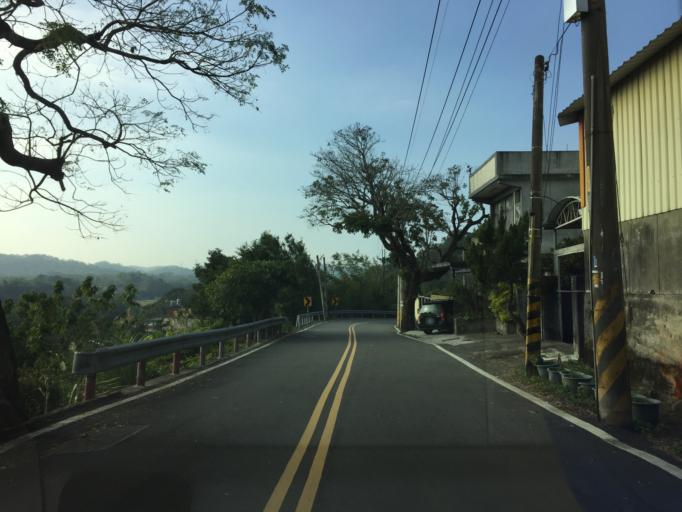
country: TW
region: Taiwan
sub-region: Hsinchu
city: Hsinchu
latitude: 24.6889
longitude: 121.0180
